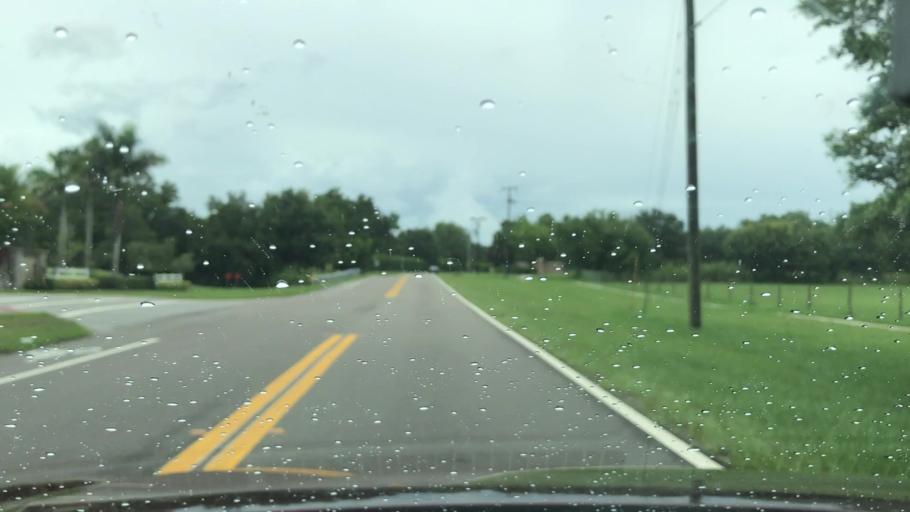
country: US
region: Florida
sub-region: Sarasota County
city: Lake Sarasota
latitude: 27.3150
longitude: -82.3998
